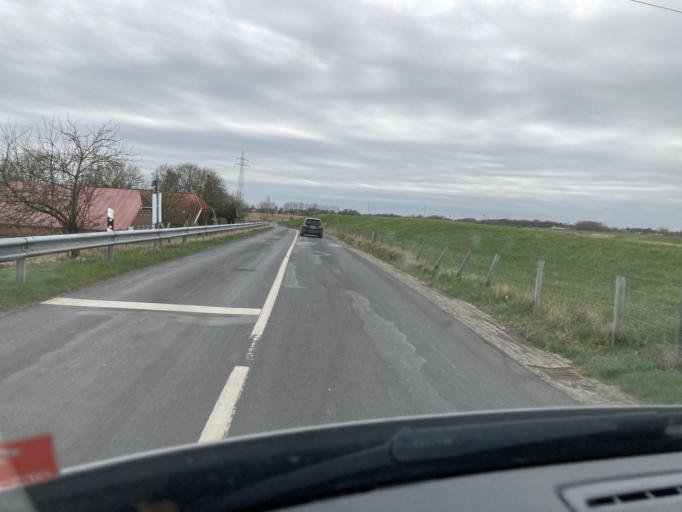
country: DE
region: Lower Saxony
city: Leer
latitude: 53.2106
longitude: 7.4652
